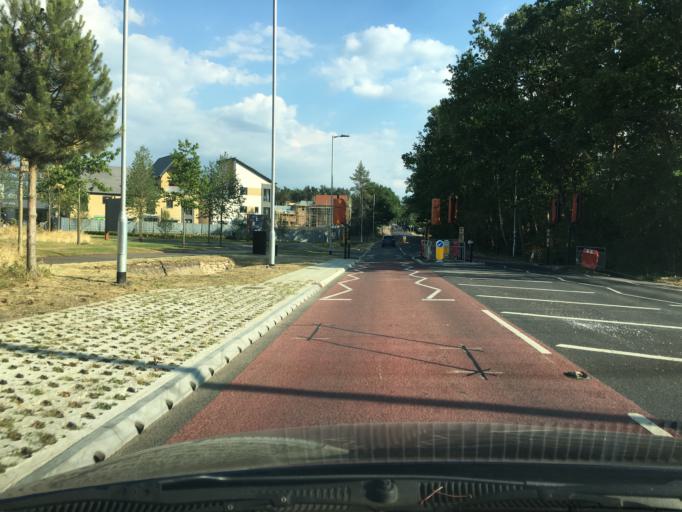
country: GB
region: England
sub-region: Bracknell Forest
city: Crowthorne
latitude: 51.3790
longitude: -0.7911
